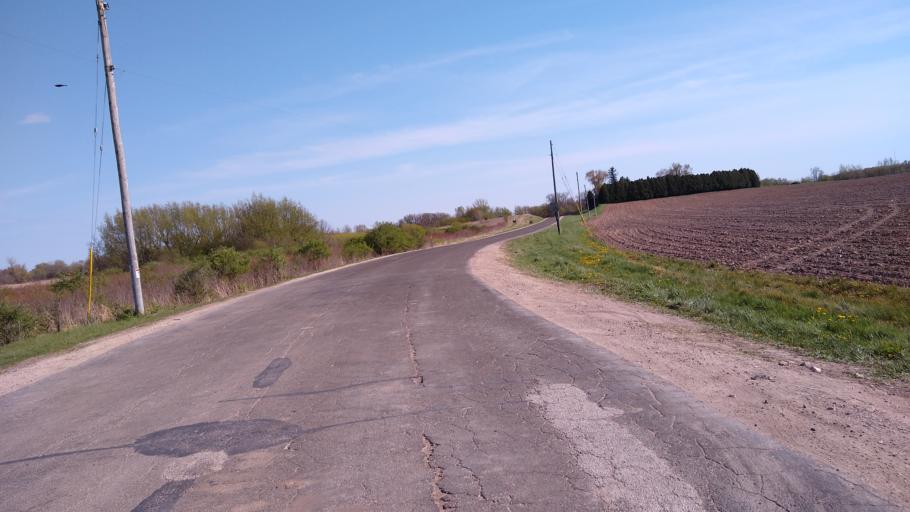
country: US
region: Wisconsin
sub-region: Dane County
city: Waunakee
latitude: 43.1460
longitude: -89.4386
